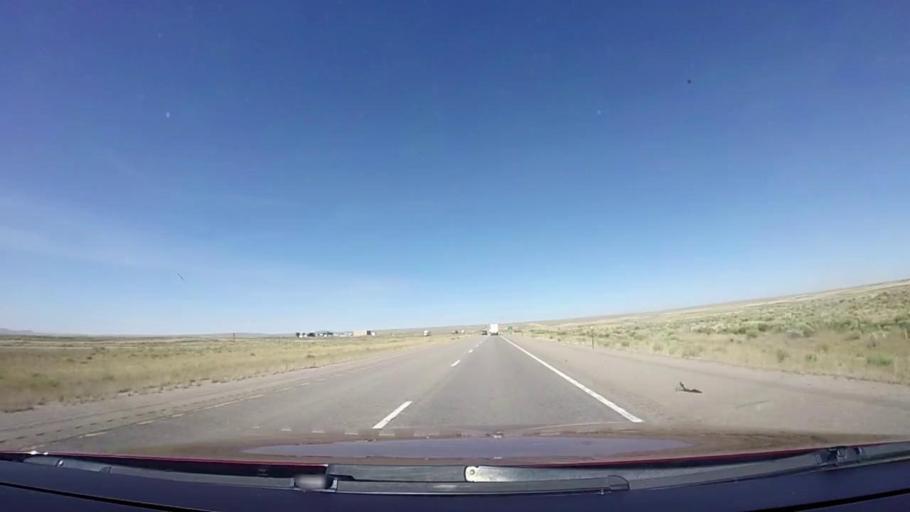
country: US
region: Wyoming
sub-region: Sweetwater County
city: Rock Springs
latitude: 41.6398
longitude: -108.4793
